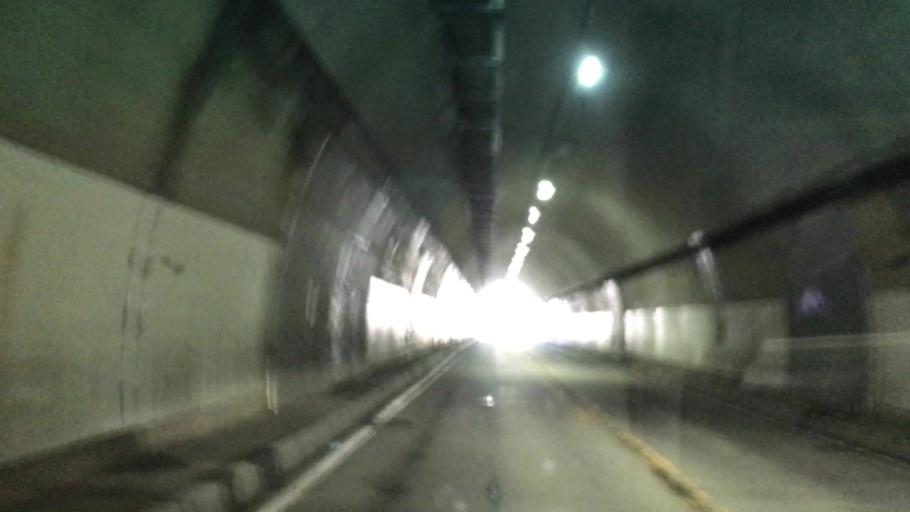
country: JP
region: Hokkaido
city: Iwanai
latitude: 43.1090
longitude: 140.4516
